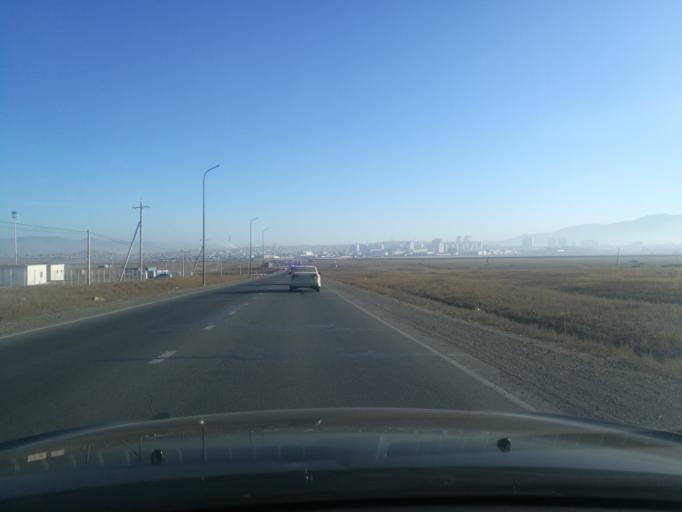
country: MN
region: Ulaanbaatar
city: Ulaanbaatar
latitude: 47.8494
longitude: 106.7385
